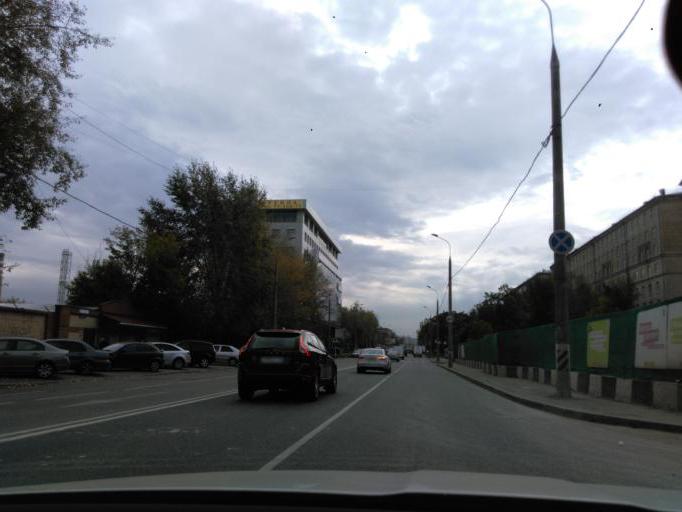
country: RU
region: Moscow
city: Ostankinskiy
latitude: 55.8193
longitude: 37.5933
